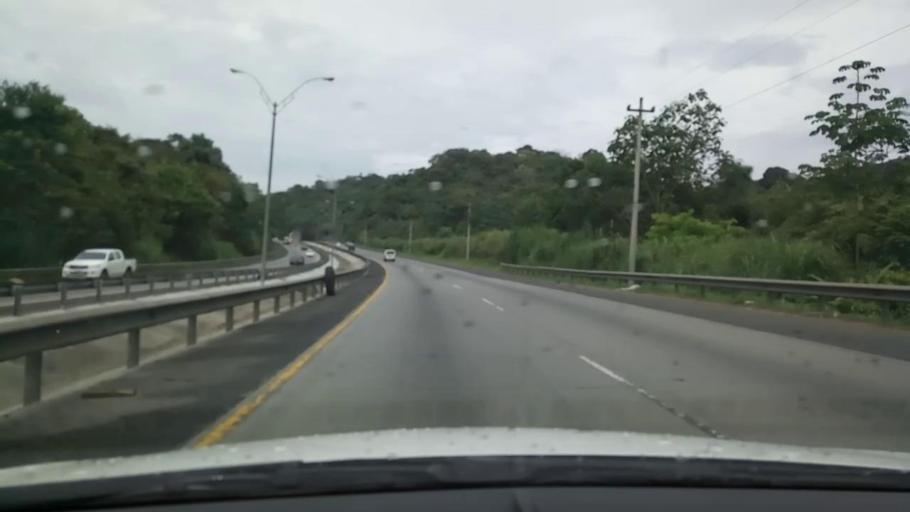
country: PA
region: Panama
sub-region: Distrito de Panama
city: Paraiso
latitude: 9.0316
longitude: -79.6150
